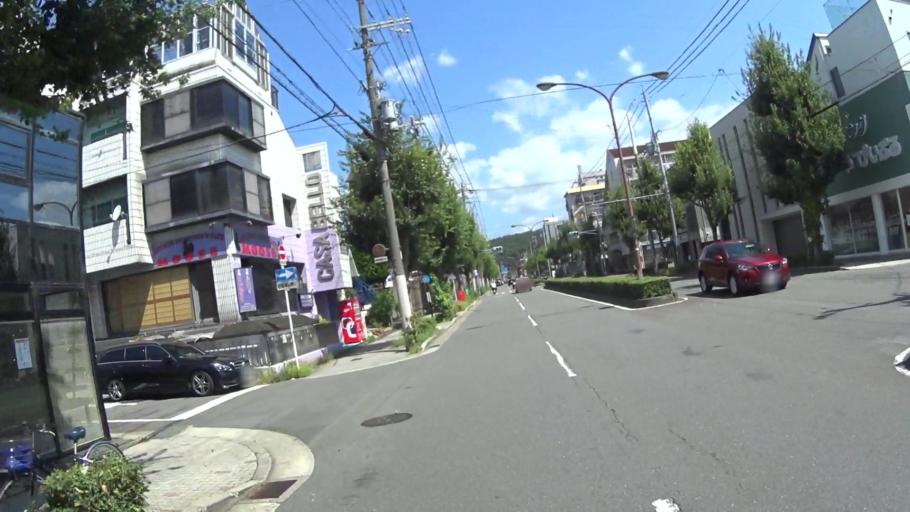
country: JP
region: Kyoto
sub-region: Kyoto-shi
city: Kamigyo-ku
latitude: 35.0484
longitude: 135.7705
